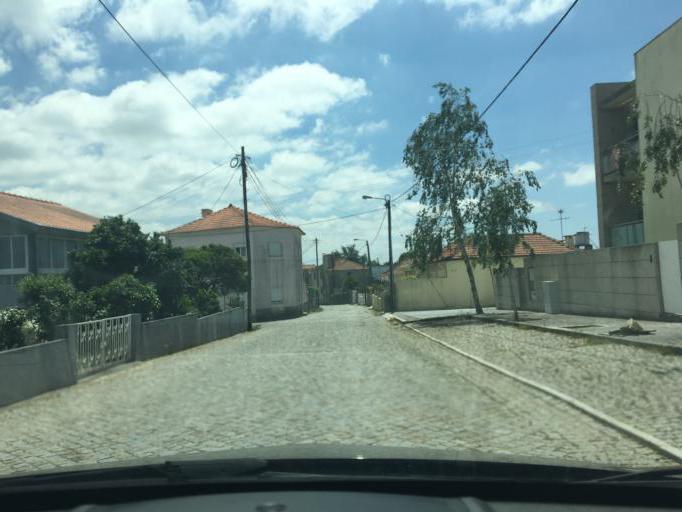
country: PT
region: Porto
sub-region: Maia
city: Anta
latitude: 41.2840
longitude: -8.6141
